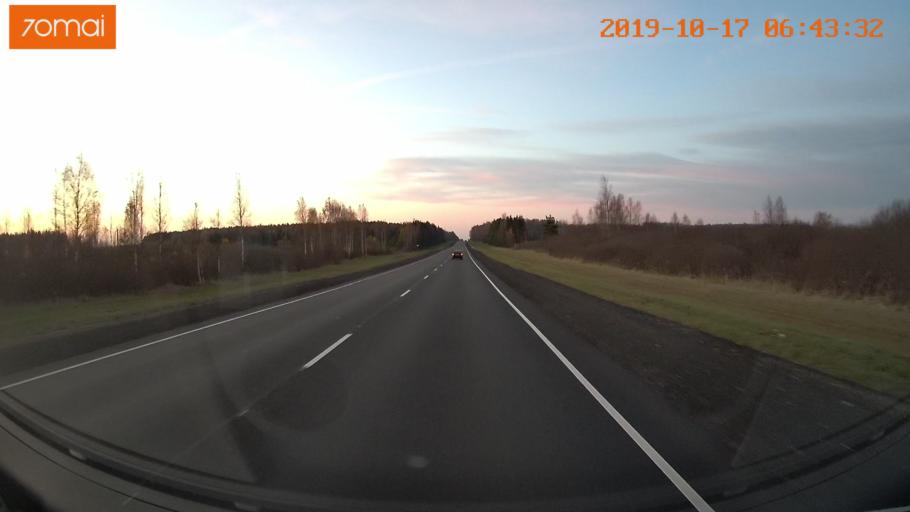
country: RU
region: Vladimir
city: Kideksha
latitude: 56.5858
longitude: 40.5551
